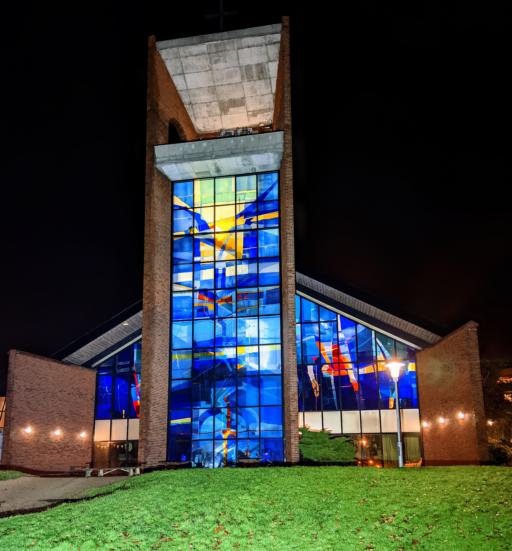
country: NO
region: Rogaland
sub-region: Time
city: Bryne
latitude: 58.7369
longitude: 5.6444
